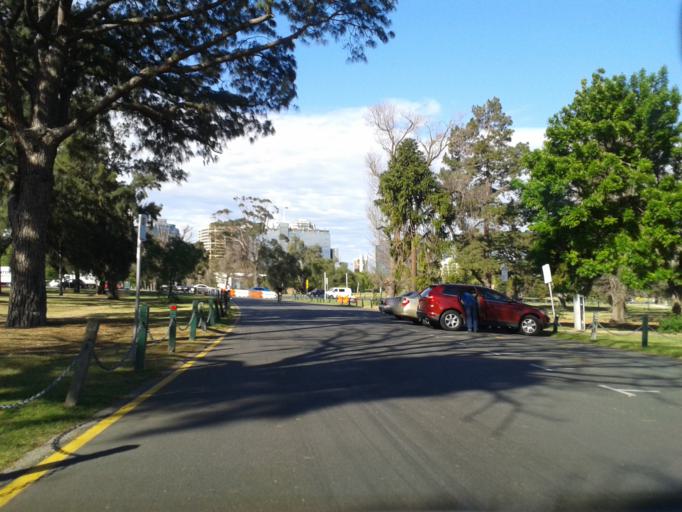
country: AU
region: Victoria
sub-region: Port Phillip
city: South Melbourne
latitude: -37.8384
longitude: 144.9668
